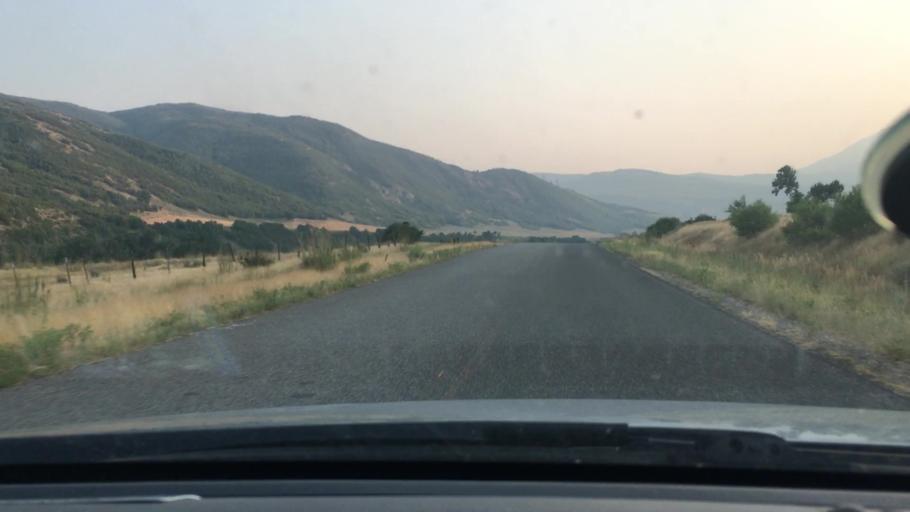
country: US
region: Utah
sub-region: Utah County
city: Mapleton
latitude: 40.0447
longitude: -111.4788
